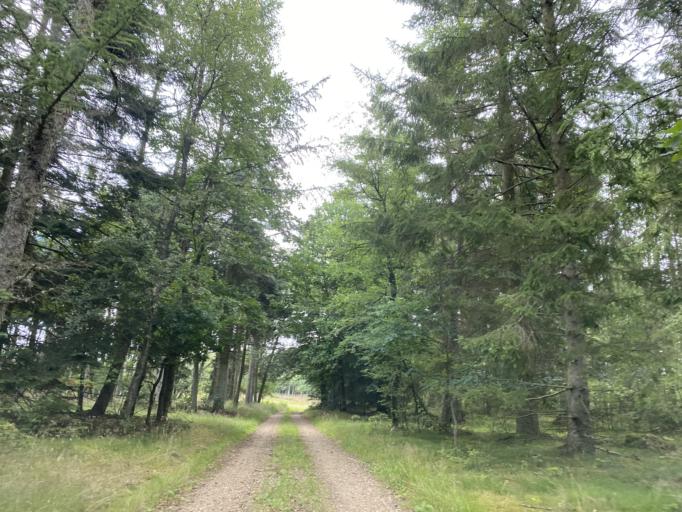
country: DK
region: Central Jutland
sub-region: Viborg Kommune
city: Bjerringbro
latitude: 56.2715
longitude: 9.6537
